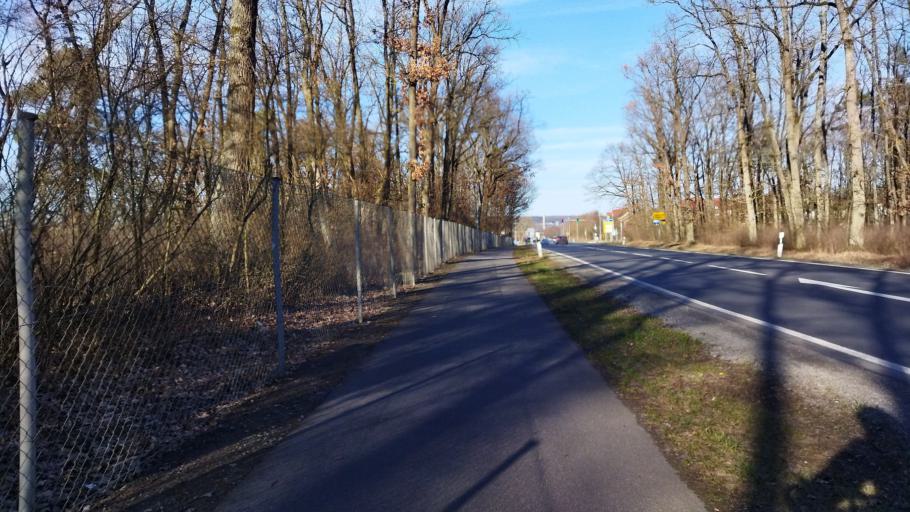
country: DE
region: Bavaria
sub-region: Regierungsbezirk Unterfranken
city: Sennfeld
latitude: 50.0325
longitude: 10.2456
